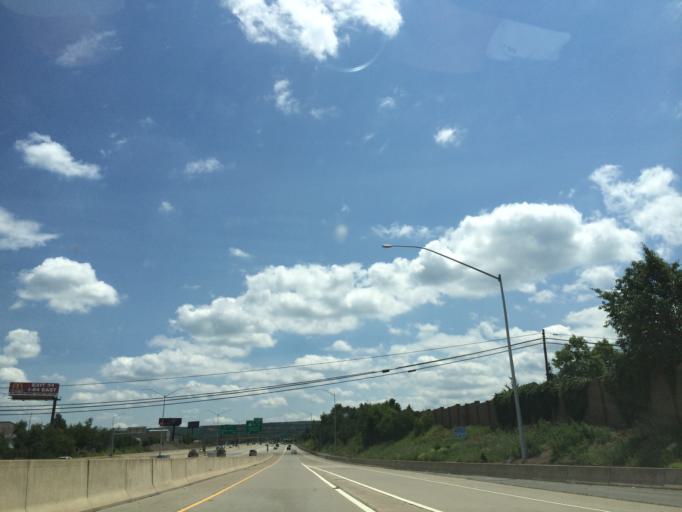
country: US
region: Pennsylvania
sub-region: Lackawanna County
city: Dunmore
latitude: 41.4299
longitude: -75.6207
